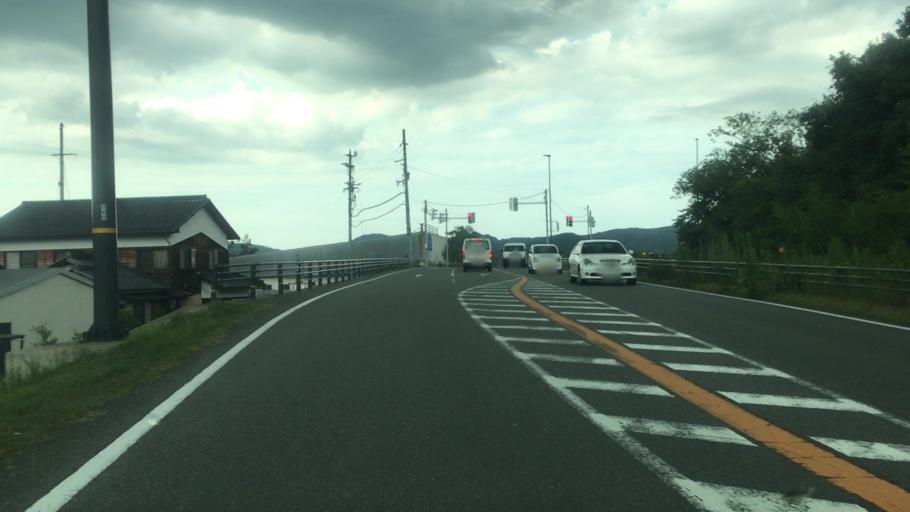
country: JP
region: Hyogo
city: Toyooka
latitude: 35.4765
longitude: 134.7864
